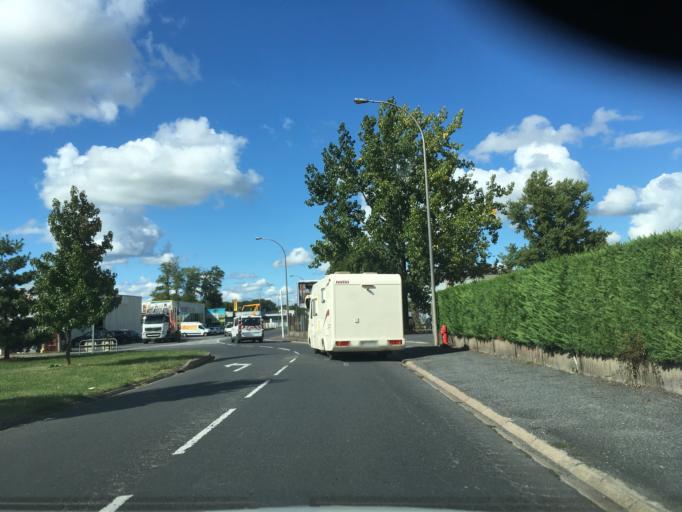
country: FR
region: Limousin
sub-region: Departement de la Correze
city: Saint-Pantaleon-de-Larche
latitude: 45.1507
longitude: 1.4816
